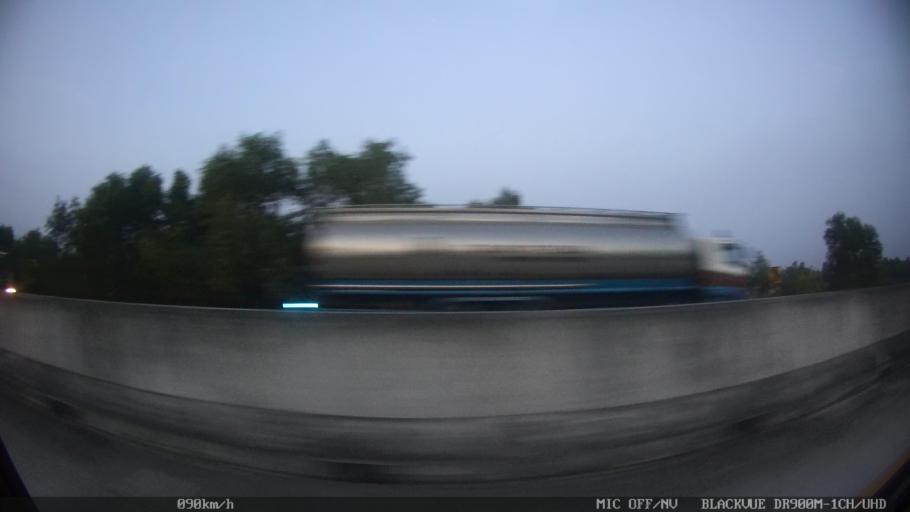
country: ID
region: Lampung
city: Sidorejo
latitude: -5.6027
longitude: 105.5545
